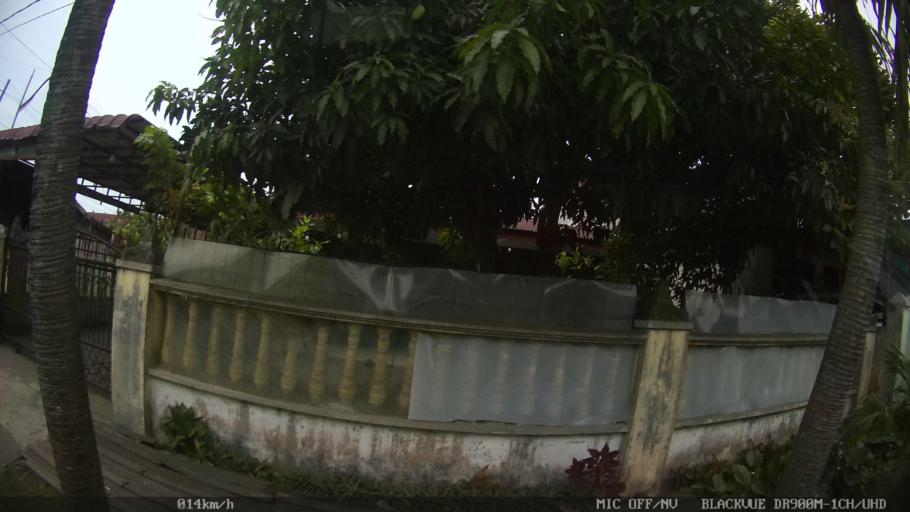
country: ID
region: North Sumatra
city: Medan
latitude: 3.5775
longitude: 98.7323
